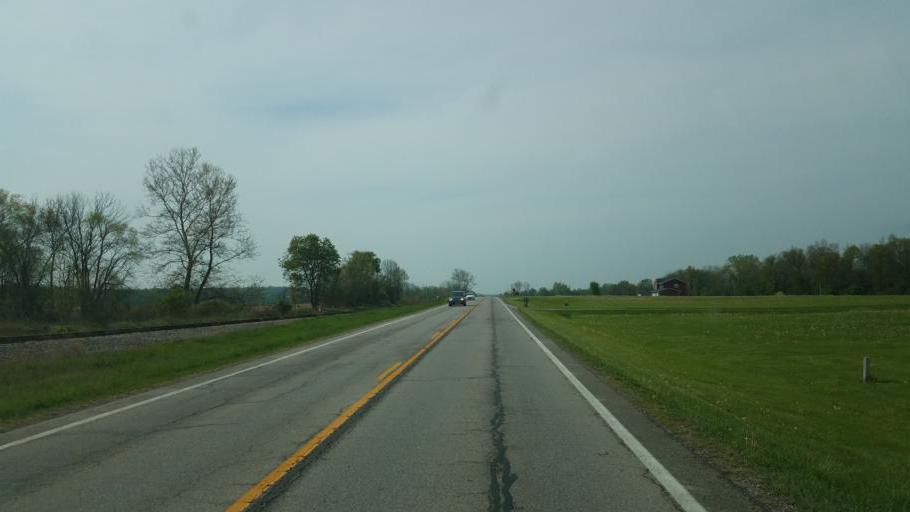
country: US
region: Ohio
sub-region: Licking County
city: Utica
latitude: 40.2756
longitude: -82.4497
